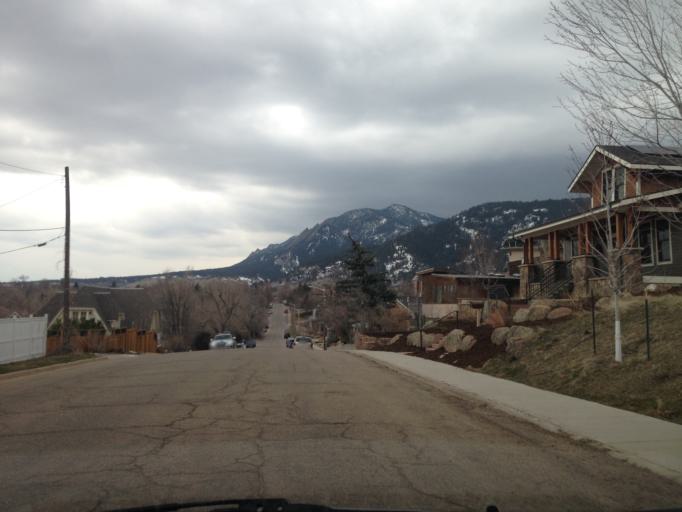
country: US
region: Colorado
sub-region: Boulder County
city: Boulder
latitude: 40.0255
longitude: -105.2916
